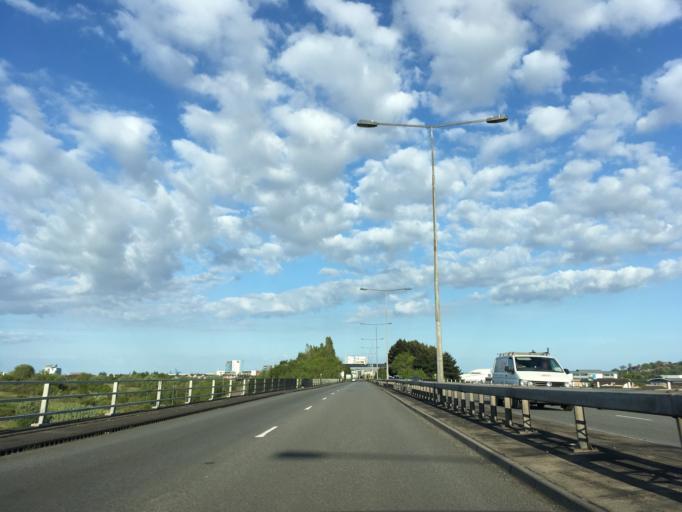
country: GB
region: Wales
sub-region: Vale of Glamorgan
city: Penarth
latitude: 51.4543
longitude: -3.1944
